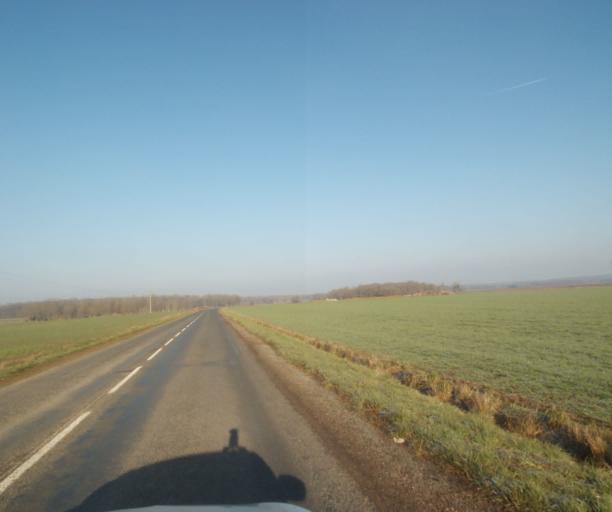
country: FR
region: Champagne-Ardenne
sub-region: Departement de la Haute-Marne
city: Montier-en-Der
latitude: 48.4991
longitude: 4.7518
